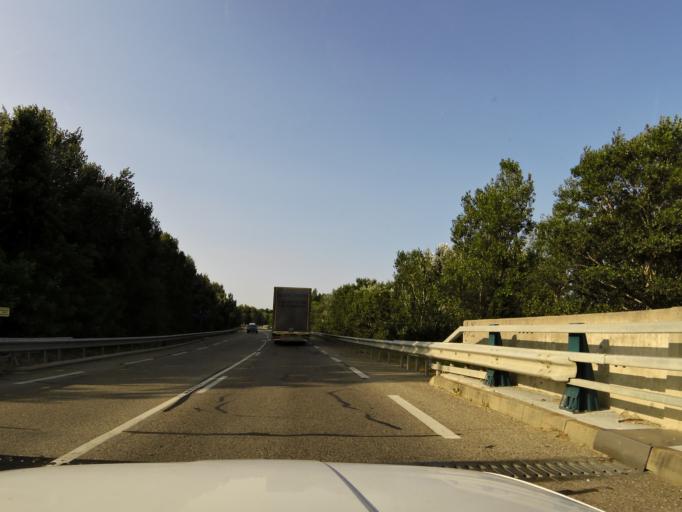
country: FR
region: Languedoc-Roussillon
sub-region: Departement du Gard
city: Pont-Saint-Esprit
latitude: 44.2557
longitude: 4.6593
